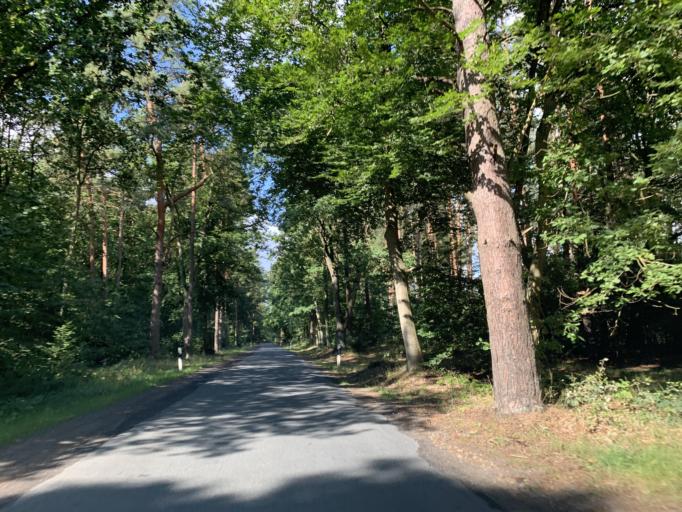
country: DE
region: Mecklenburg-Vorpommern
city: Carpin
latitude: 53.3825
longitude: 13.2031
